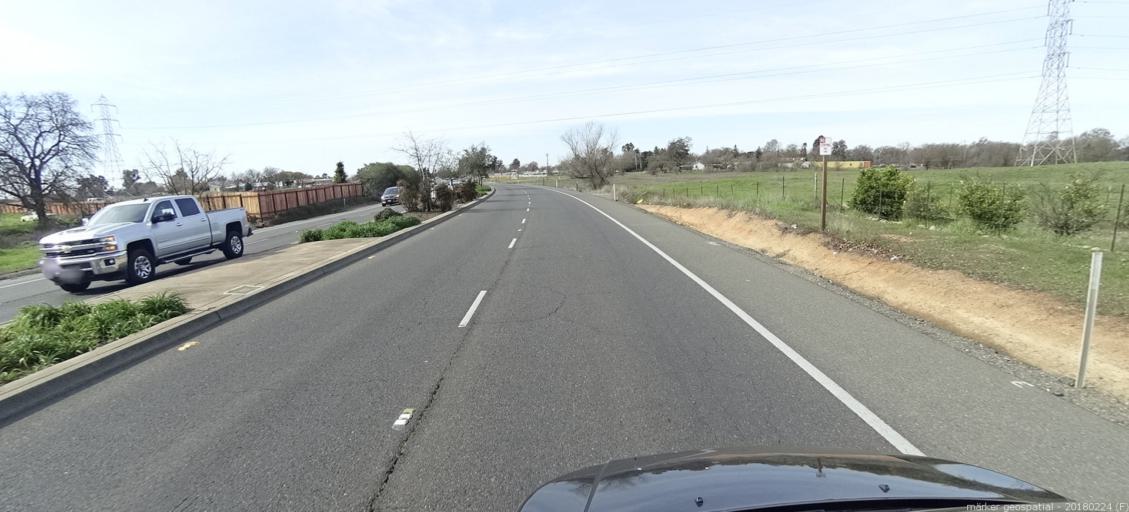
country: US
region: California
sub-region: Sacramento County
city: Rio Linda
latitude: 38.6901
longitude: -121.4264
